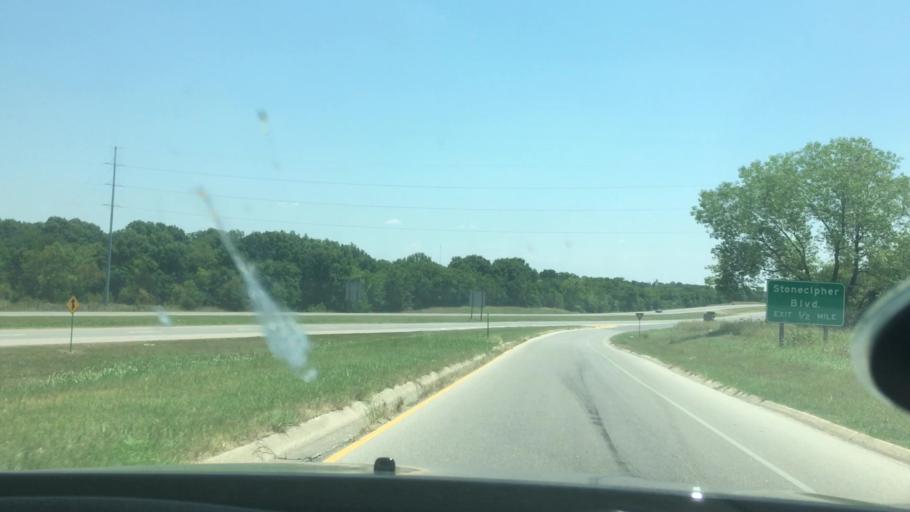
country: US
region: Oklahoma
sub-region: Pontotoc County
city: Ada
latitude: 34.7460
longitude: -96.6531
